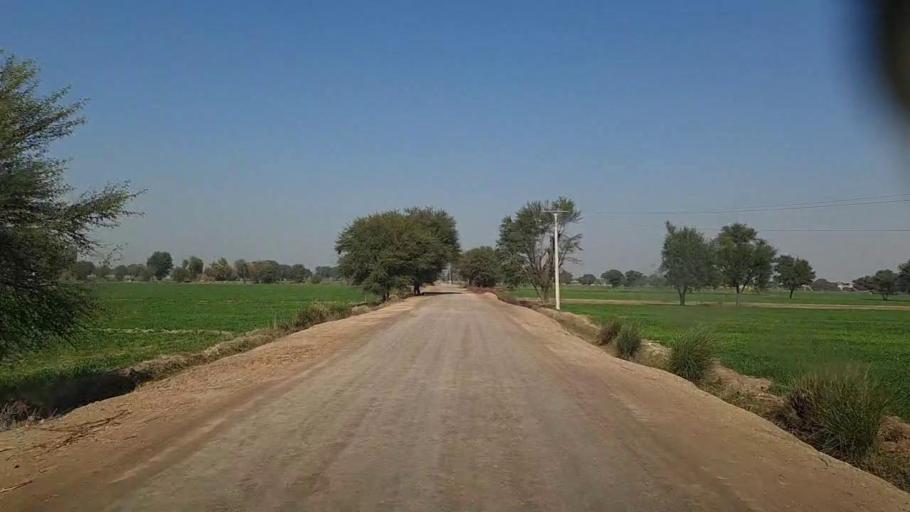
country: PK
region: Sindh
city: Khairpur
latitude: 27.9960
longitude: 69.8496
